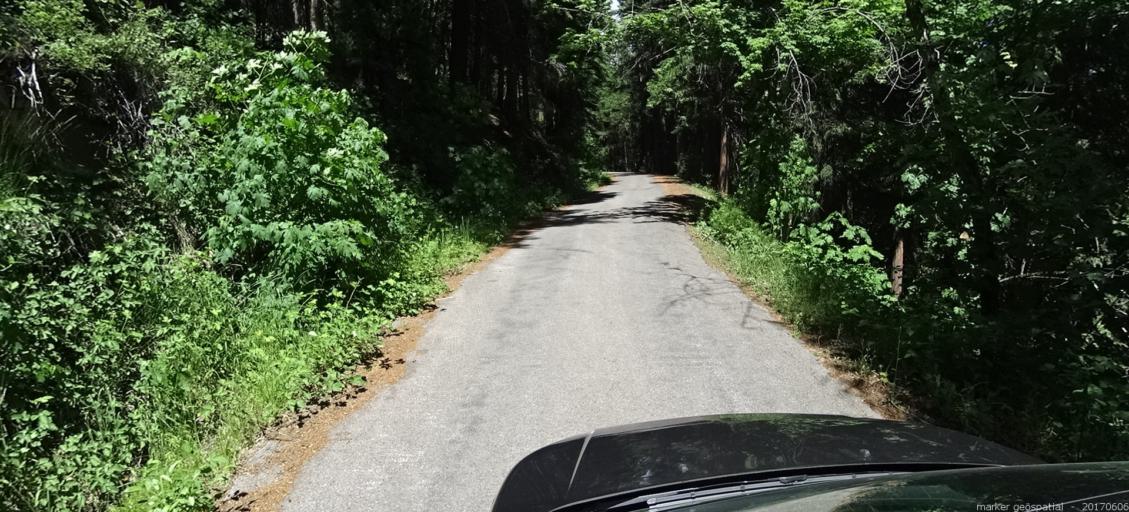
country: US
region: California
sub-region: Siskiyou County
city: Mount Shasta
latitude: 41.2714
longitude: -122.3039
